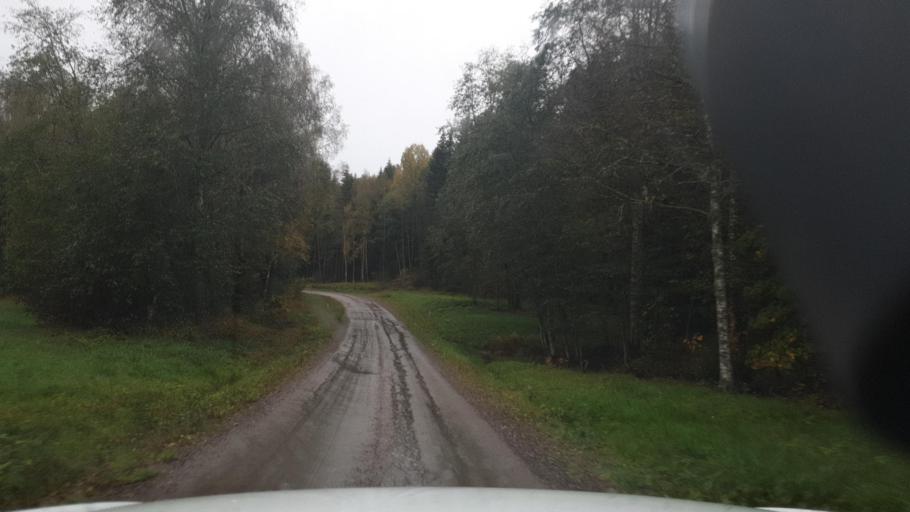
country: SE
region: Vaermland
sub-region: Eda Kommun
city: Amotfors
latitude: 59.7870
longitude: 12.4273
